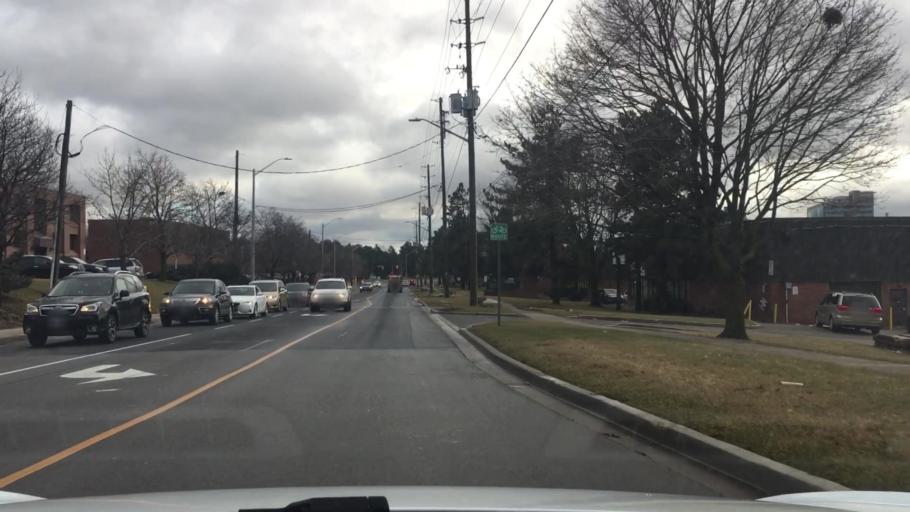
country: CA
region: Ontario
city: Willowdale
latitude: 43.8209
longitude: -79.3446
